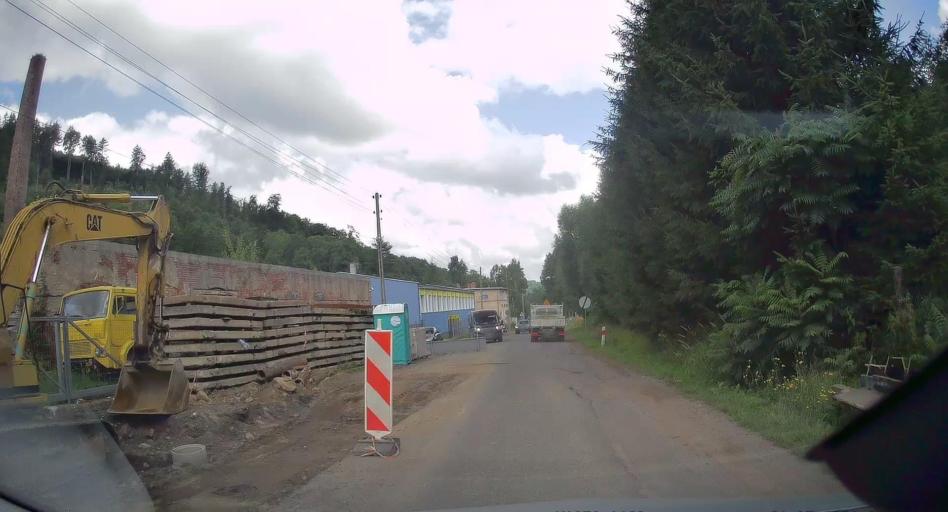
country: PL
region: Lower Silesian Voivodeship
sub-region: Powiat walbrzyski
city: Walim
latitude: 50.7203
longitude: 16.4168
